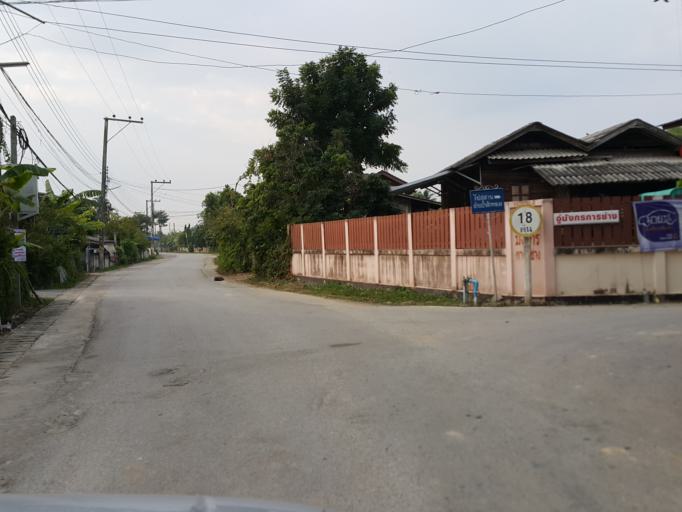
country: TH
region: Chiang Mai
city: San Kamphaeng
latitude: 18.8097
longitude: 99.1042
